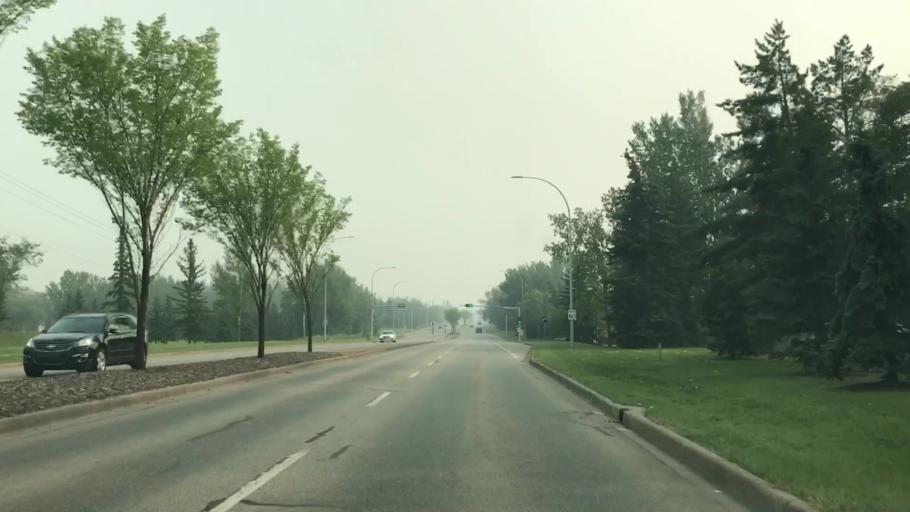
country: CA
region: Alberta
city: Sherwood Park
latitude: 53.5304
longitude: -113.3202
